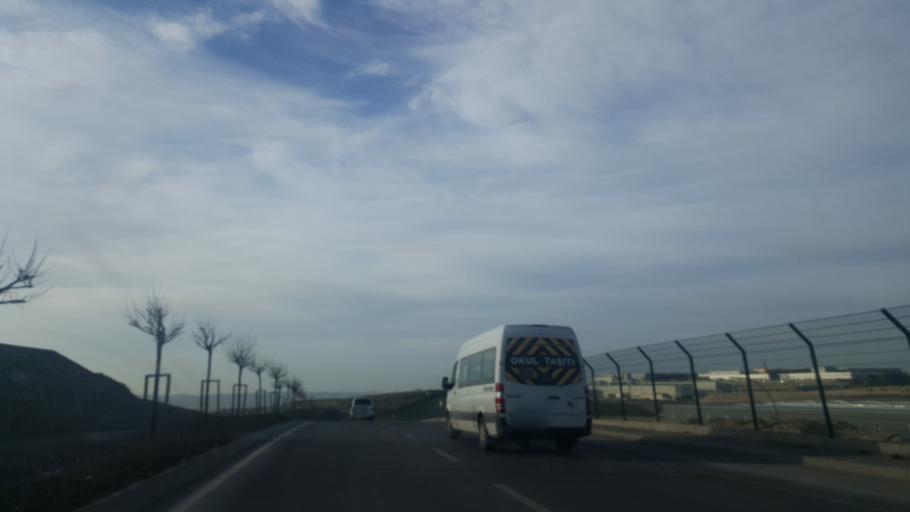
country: TR
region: Kocaeli
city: Tavsanli
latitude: 40.8215
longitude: 29.5602
